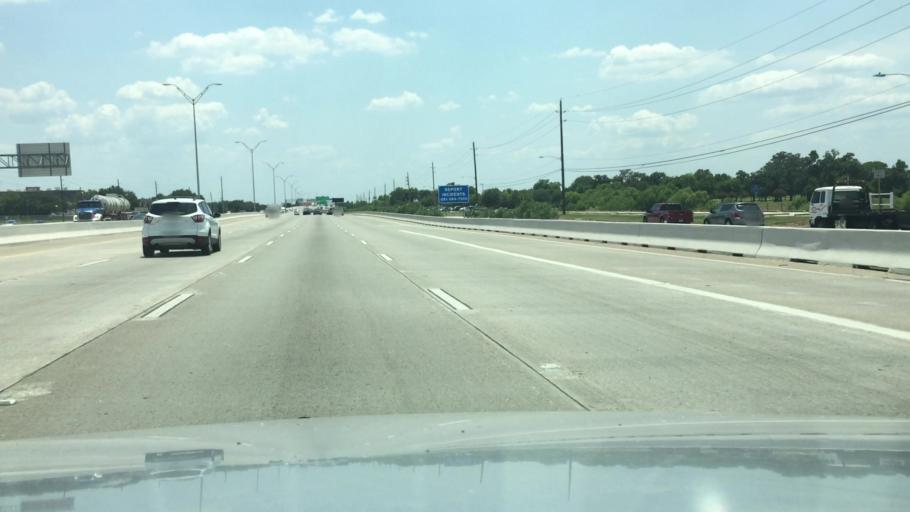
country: US
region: Texas
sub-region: Fort Bend County
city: Meadows Place
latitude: 29.6998
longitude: -95.5573
